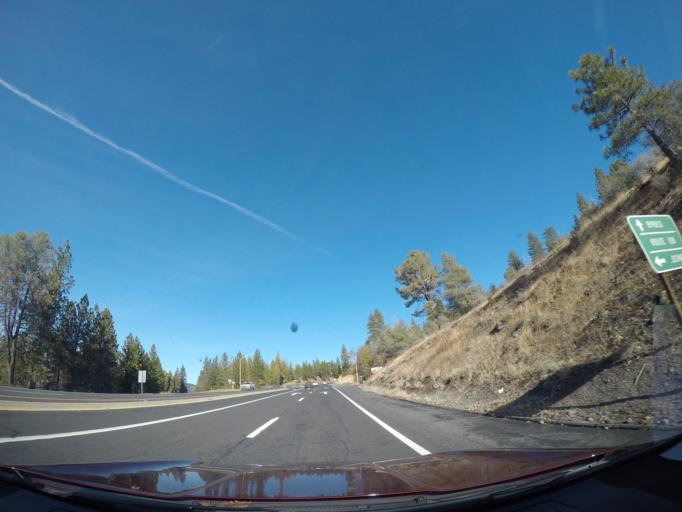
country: US
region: California
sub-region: Tuolumne County
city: Twain Harte
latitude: 38.0190
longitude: -120.2472
